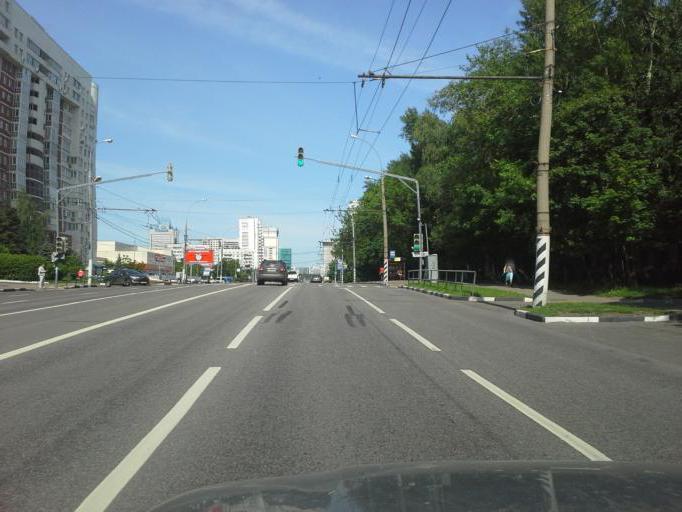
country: RU
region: Moscow
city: Zyuzino
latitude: 55.6550
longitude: 37.5761
